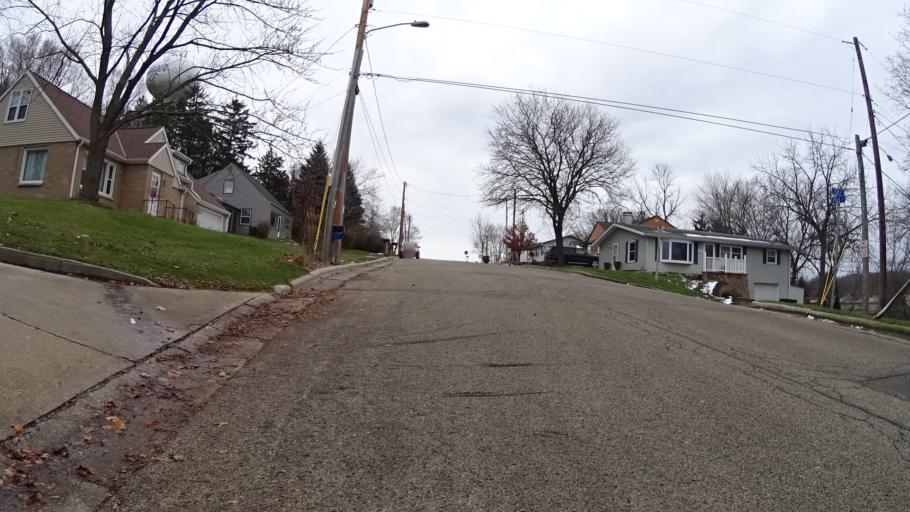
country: US
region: Wisconsin
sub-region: Washington County
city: Slinger
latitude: 43.3330
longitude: -88.2859
